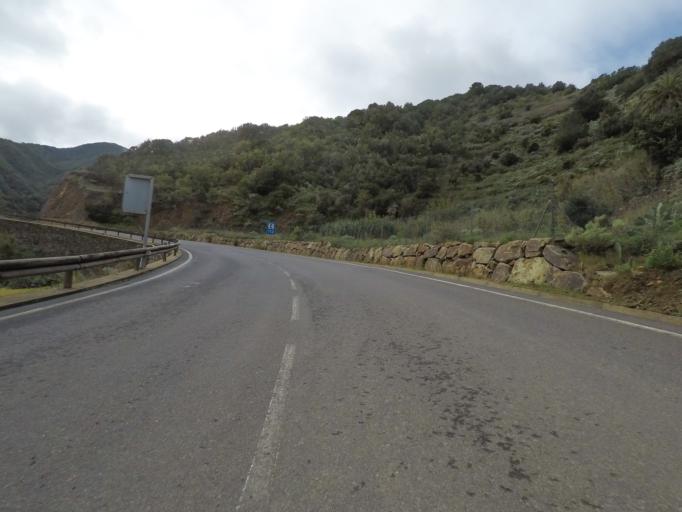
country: ES
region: Canary Islands
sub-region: Provincia de Santa Cruz de Tenerife
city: Vallehermosa
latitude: 28.1645
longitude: -17.2830
